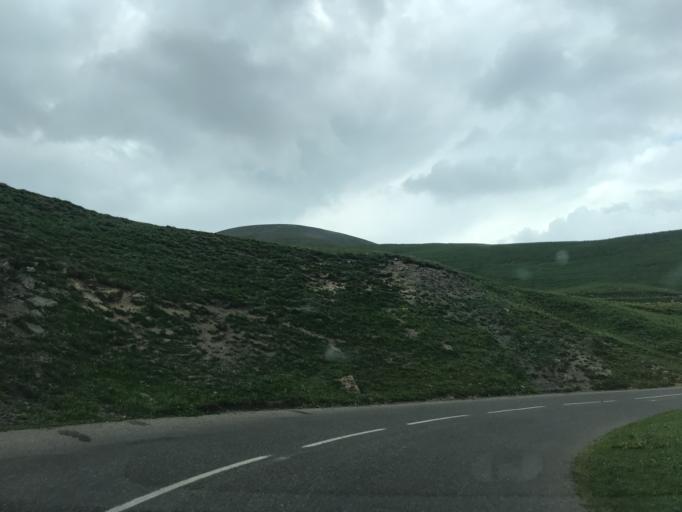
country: FR
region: Rhone-Alpes
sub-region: Departement de la Savoie
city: Valloire
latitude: 45.0797
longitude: 6.4220
